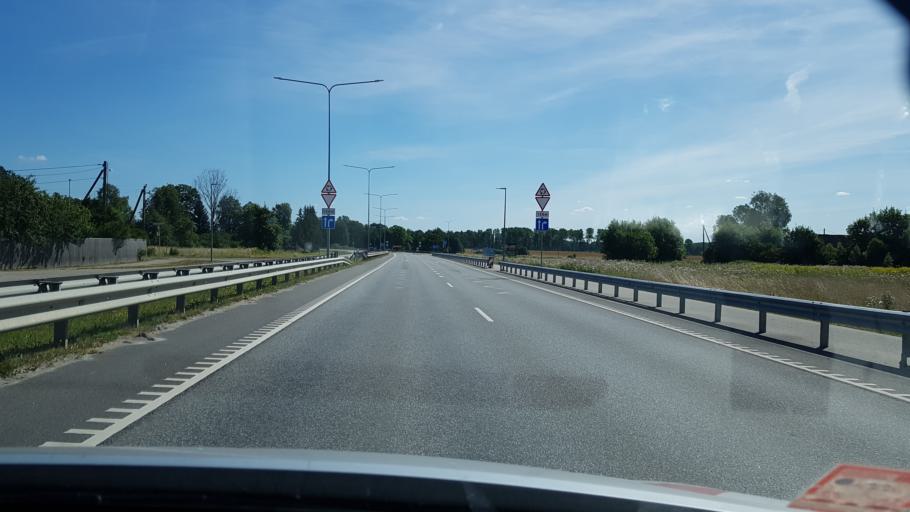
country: EE
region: Tartu
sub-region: Tartu linn
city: Tartu
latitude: 58.3731
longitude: 26.7962
